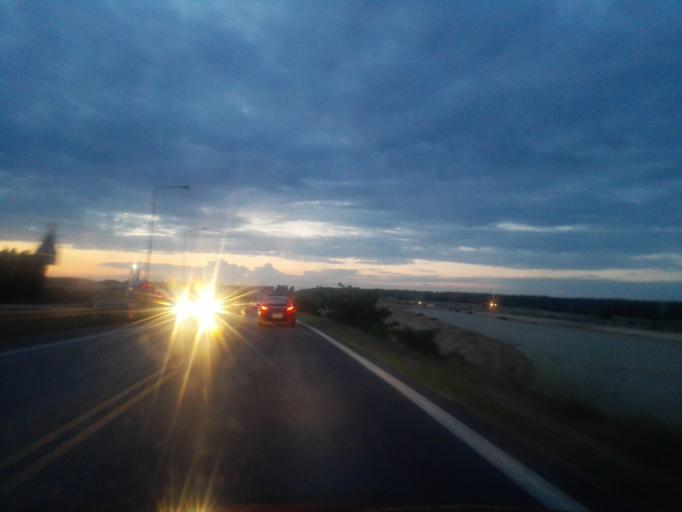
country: PL
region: Lodz Voivodeship
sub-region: Powiat piotrkowski
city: Czarnocin
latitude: 51.5465
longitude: 19.6033
